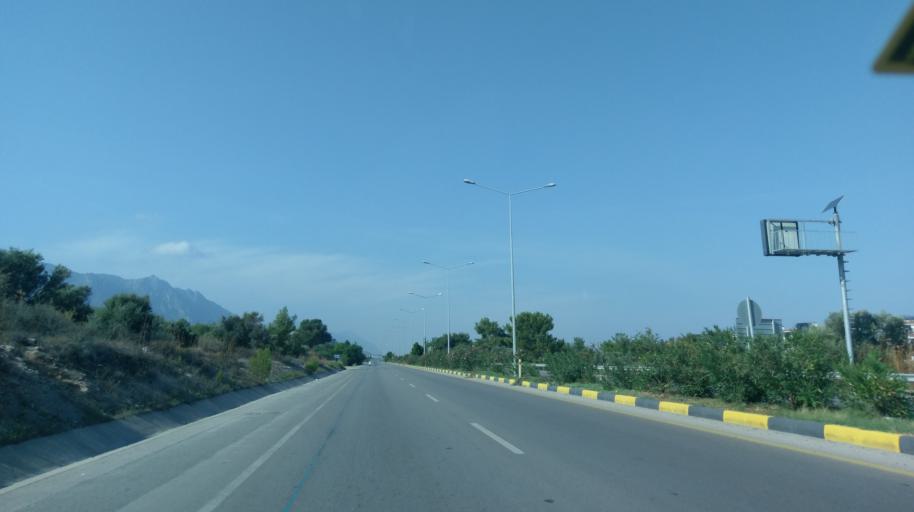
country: CY
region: Keryneia
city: Kyrenia
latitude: 35.3276
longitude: 33.3063
